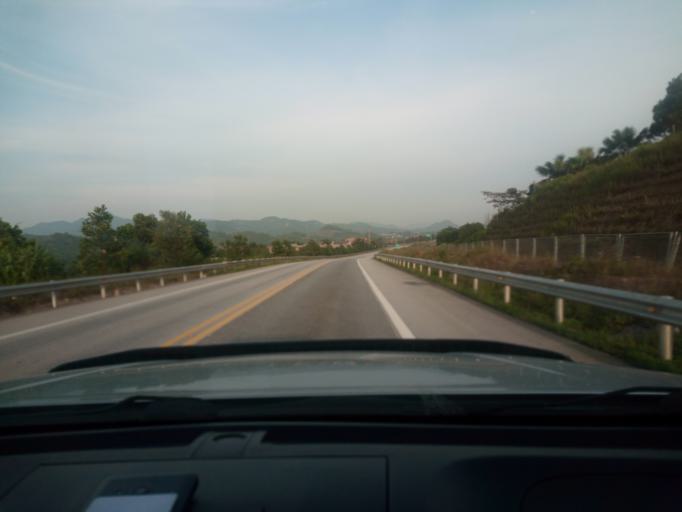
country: VN
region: Yen Bai
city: Co Phuc
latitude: 21.8861
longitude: 104.6627
